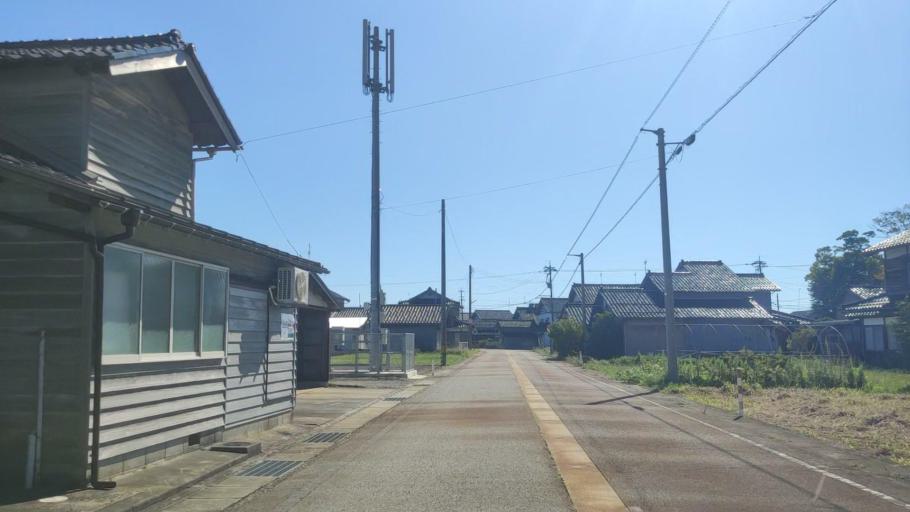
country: JP
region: Ishikawa
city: Nanao
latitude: 37.4483
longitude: 137.2898
